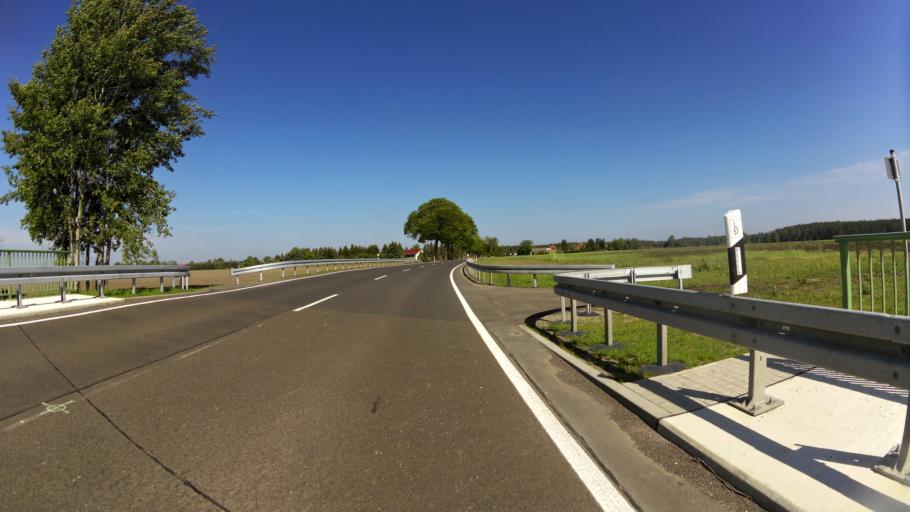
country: DE
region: Brandenburg
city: Grunewald
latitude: 51.3973
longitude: 14.0079
